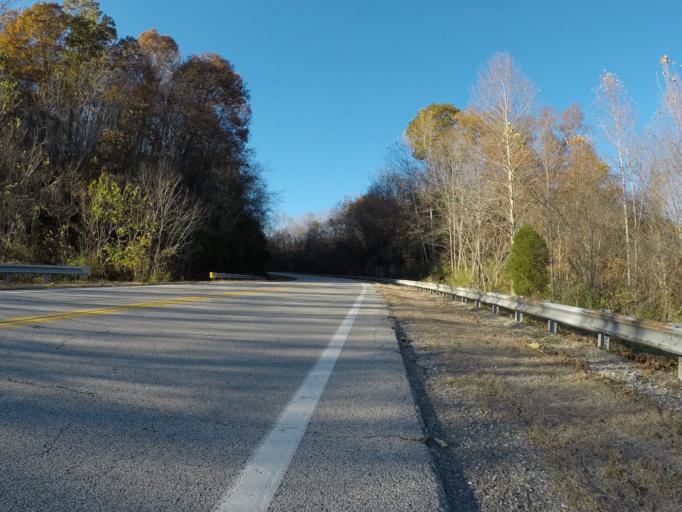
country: US
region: West Virginia
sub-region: Wayne County
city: Ceredo
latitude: 38.3809
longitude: -82.5637
